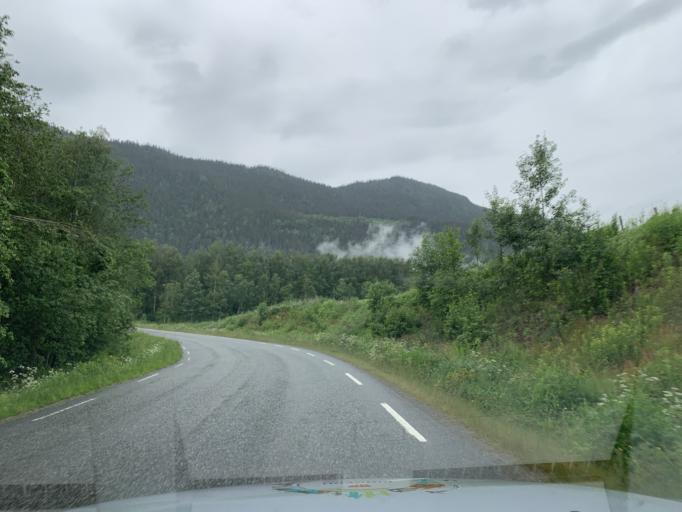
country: NO
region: Oppland
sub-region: Ringebu
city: Ringebu
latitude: 61.4489
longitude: 10.1744
